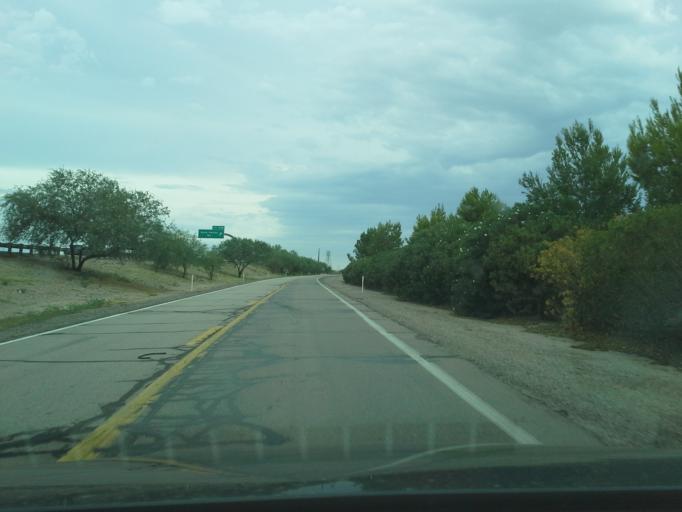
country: US
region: Arizona
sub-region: Pima County
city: Marana
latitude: 32.4036
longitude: -111.1354
